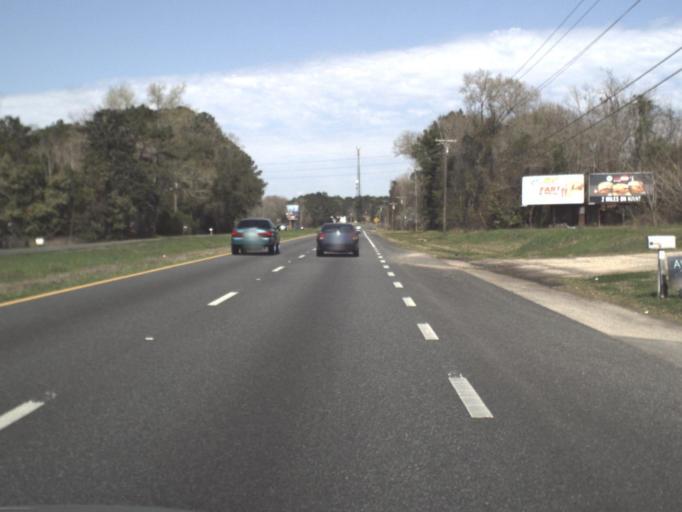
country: US
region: Florida
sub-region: Gadsden County
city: Havana
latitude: 30.6004
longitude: -84.4182
